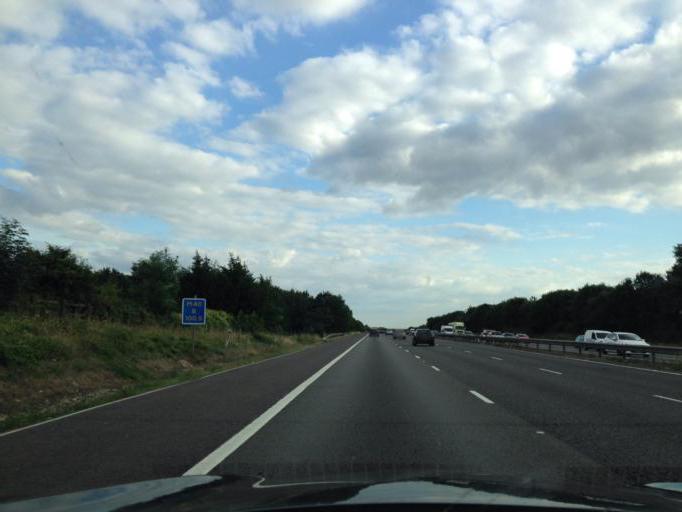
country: GB
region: England
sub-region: Oxfordshire
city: Bicester
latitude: 51.9011
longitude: -1.2059
